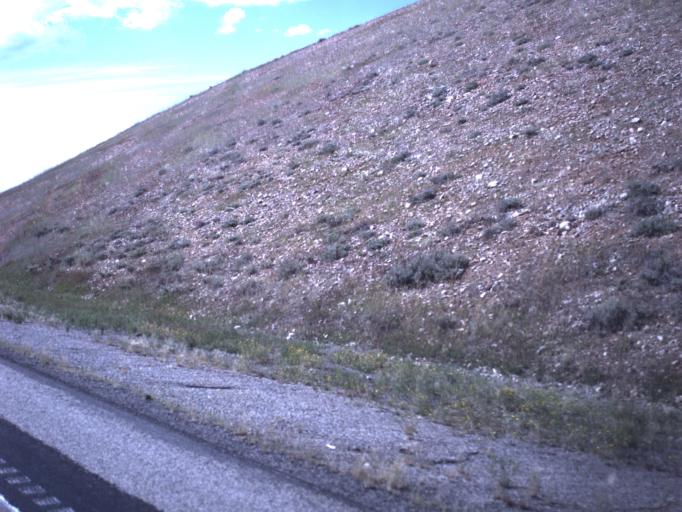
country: US
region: Utah
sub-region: Wasatch County
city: Heber
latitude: 40.2313
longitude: -111.1292
